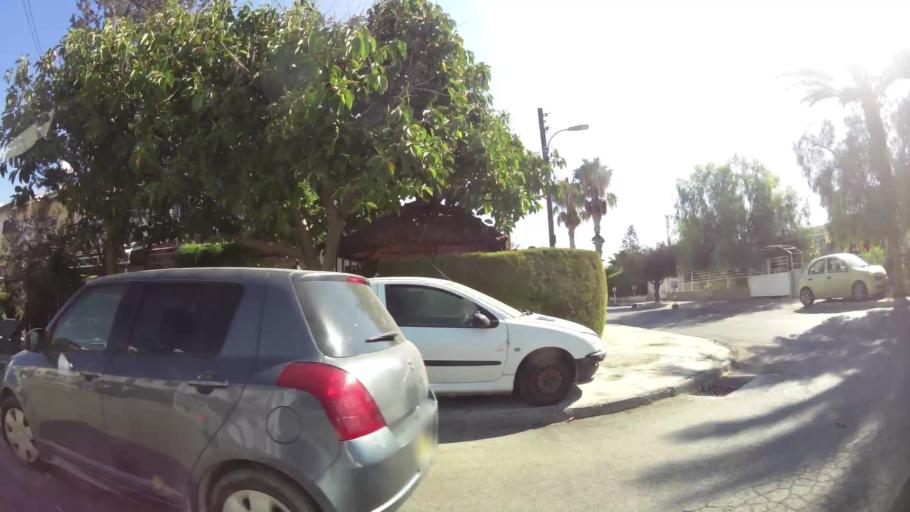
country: CY
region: Lefkosia
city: Nicosia
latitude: 35.2084
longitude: 33.3391
